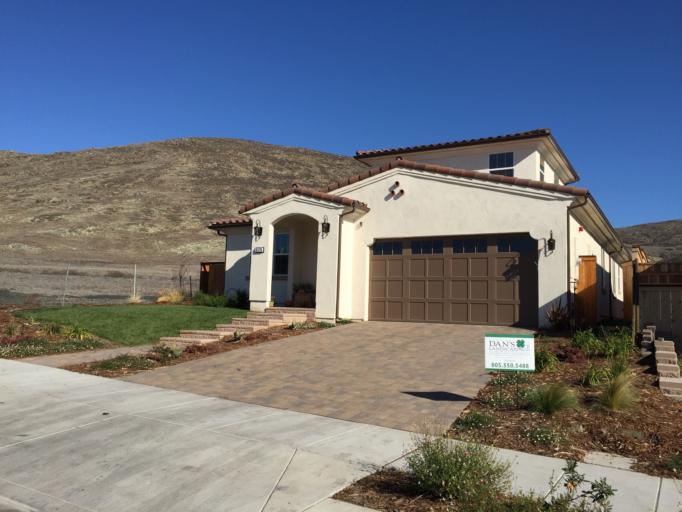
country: US
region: California
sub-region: San Luis Obispo County
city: San Luis Obispo
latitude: 35.2575
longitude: -120.6610
